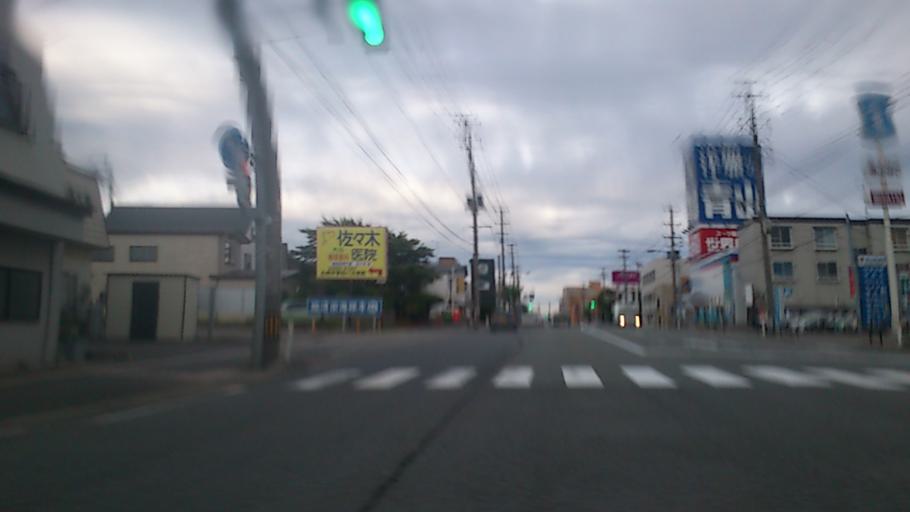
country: JP
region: Akita
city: Akita Shi
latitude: 39.7495
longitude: 140.0702
